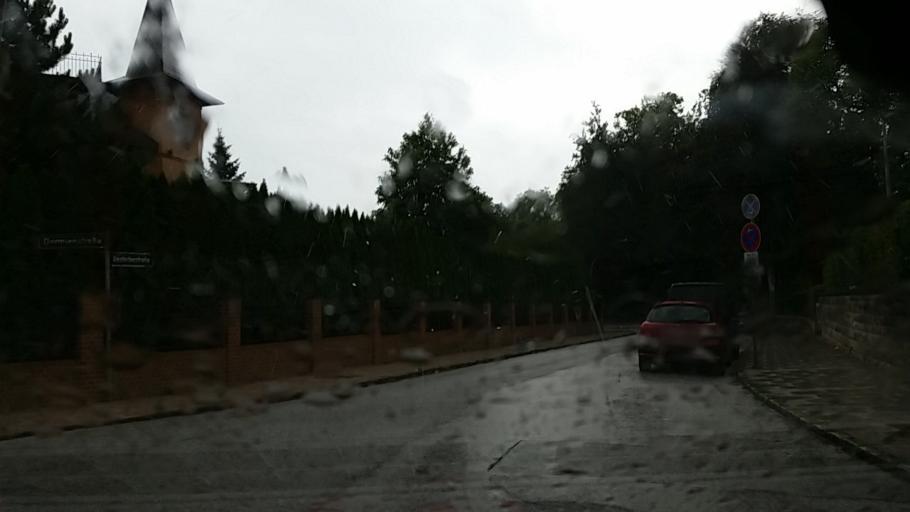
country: DE
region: Schleswig-Holstein
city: Halstenbek
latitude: 53.5621
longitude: 9.8079
